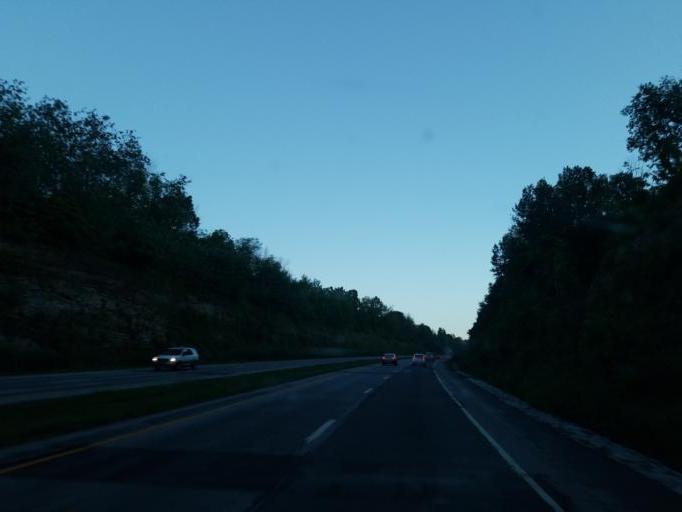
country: US
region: Ohio
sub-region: Summit County
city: Clinton
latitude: 40.9358
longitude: -81.6549
